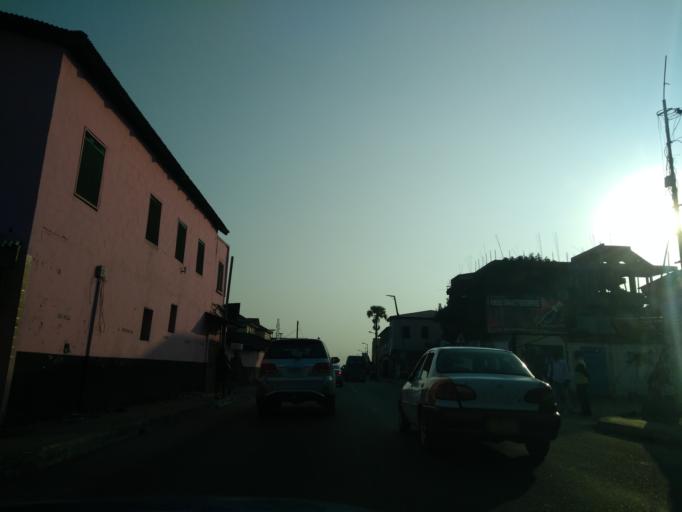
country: GH
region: Greater Accra
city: Accra
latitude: 5.5415
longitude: -0.2117
